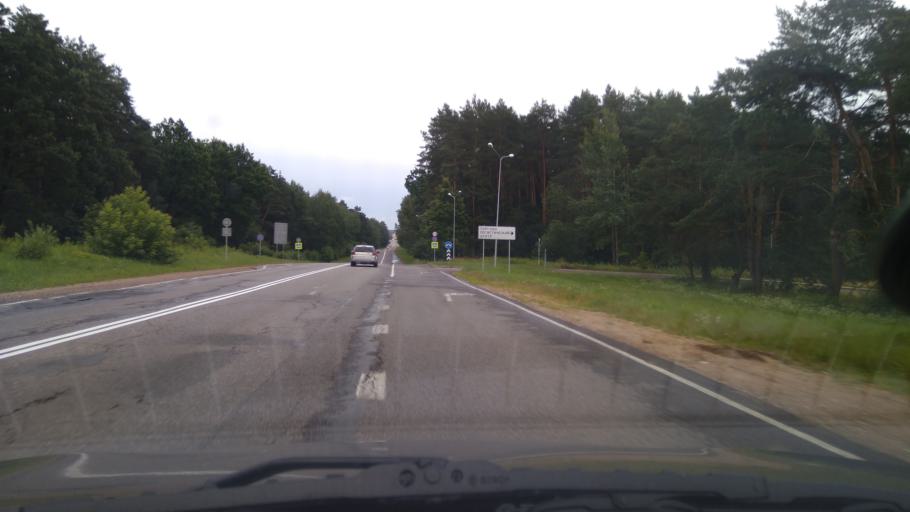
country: BY
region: Minsk
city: Bal'shavik
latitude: 53.9846
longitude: 27.5424
